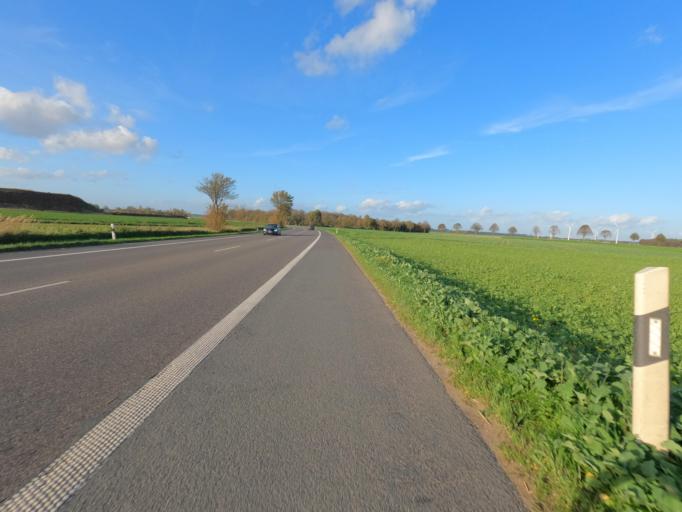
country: DE
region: North Rhine-Westphalia
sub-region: Regierungsbezirk Koln
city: Titz
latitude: 51.0480
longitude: 6.3944
